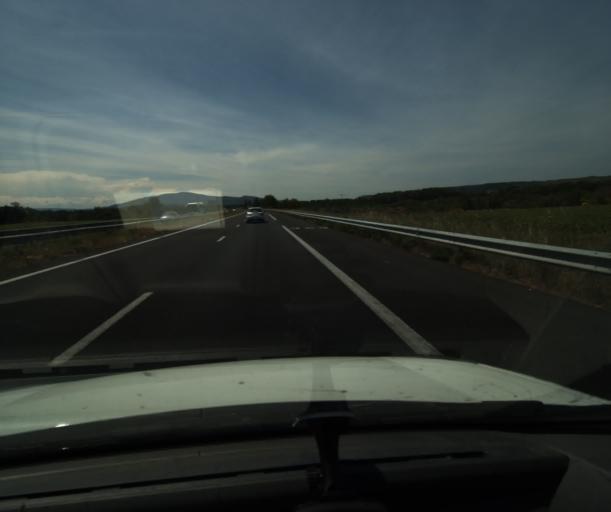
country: FR
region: Languedoc-Roussillon
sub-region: Departement de l'Aude
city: Lezignan-Corbieres
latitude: 43.1705
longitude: 2.7556
